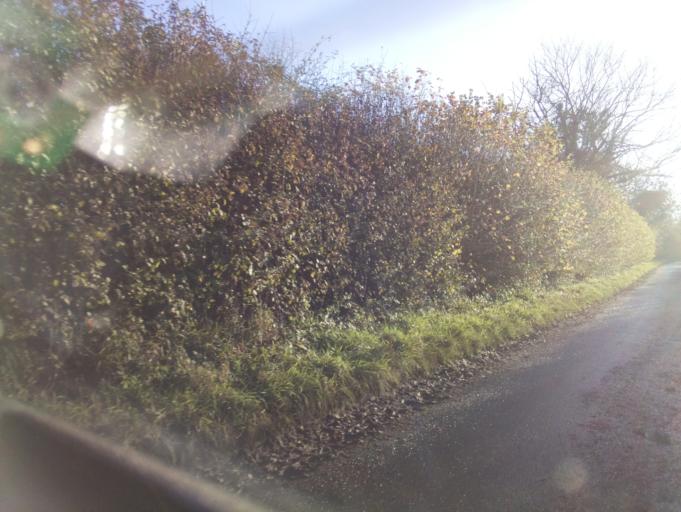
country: GB
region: England
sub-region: Somerset
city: Milborne Port
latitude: 50.9899
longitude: -2.4666
